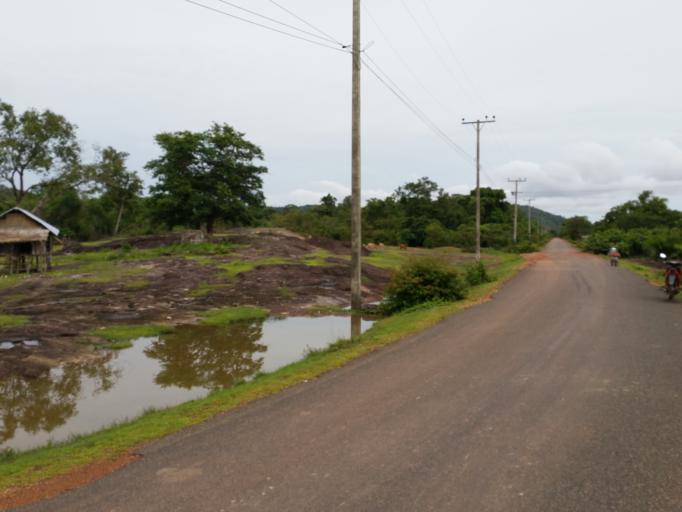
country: LA
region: Champasak
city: Khong
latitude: 14.1589
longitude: 105.7922
